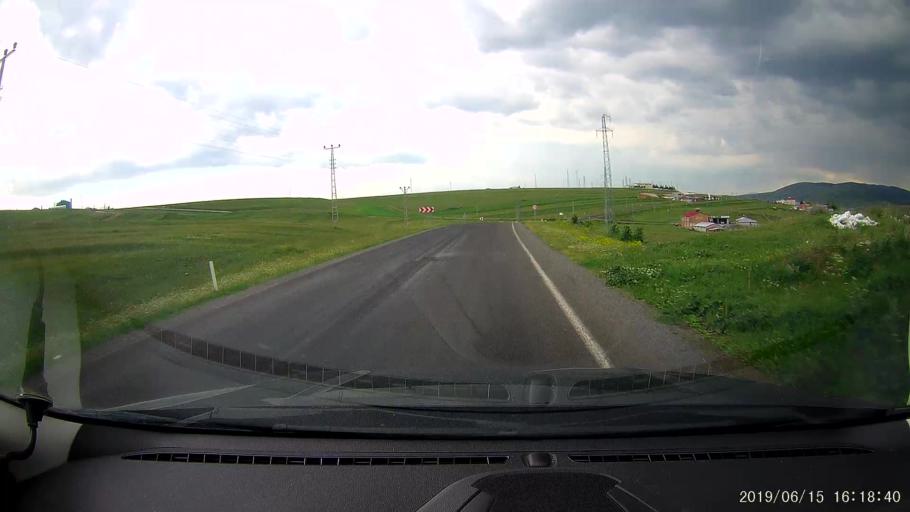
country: TR
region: Ardahan
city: Hanak
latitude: 41.2371
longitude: 42.8526
